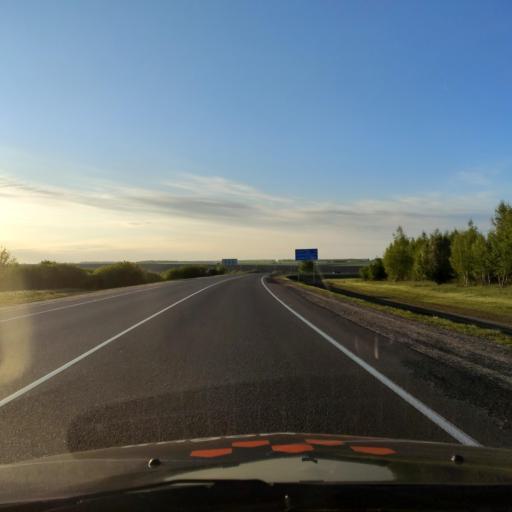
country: RU
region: Orjol
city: Livny
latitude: 52.4493
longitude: 37.6293
